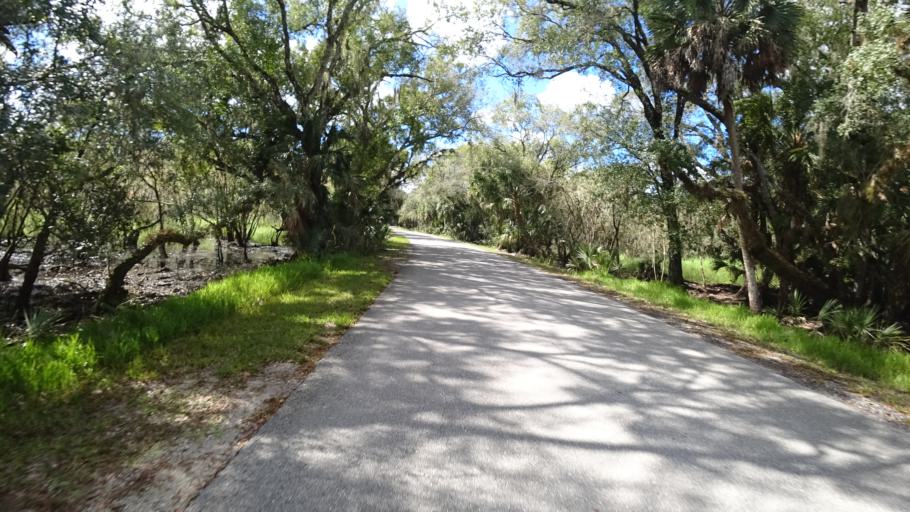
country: US
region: Florida
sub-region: Sarasota County
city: Lake Sarasota
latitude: 27.2473
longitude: -82.2999
